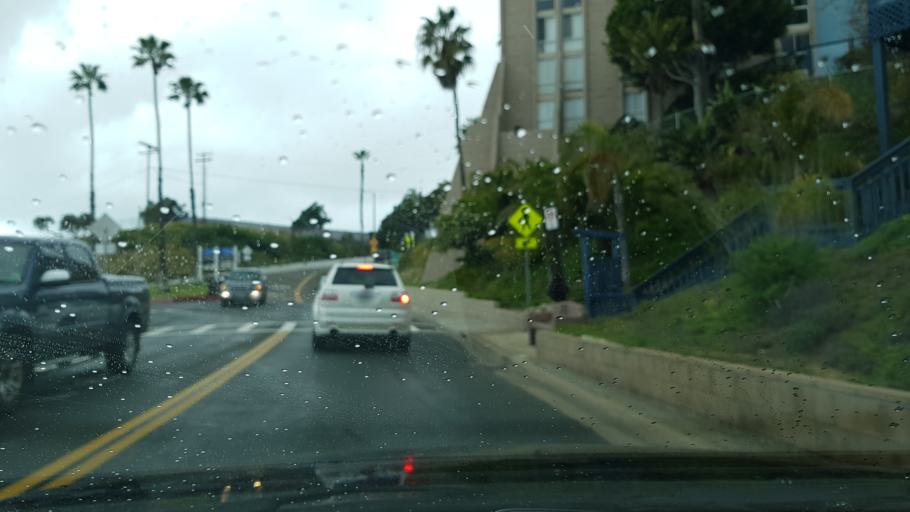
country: US
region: California
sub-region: San Diego County
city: Oceanside
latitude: 33.2068
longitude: -117.3894
